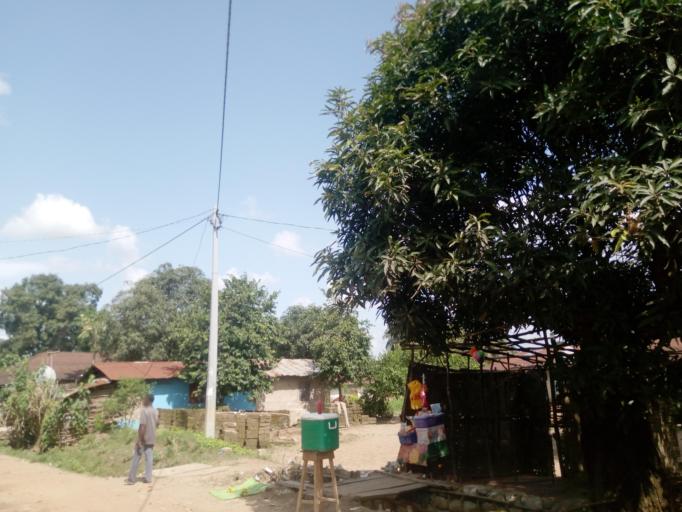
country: SL
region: Northern Province
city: Makeni
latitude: 8.8878
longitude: -12.0395
